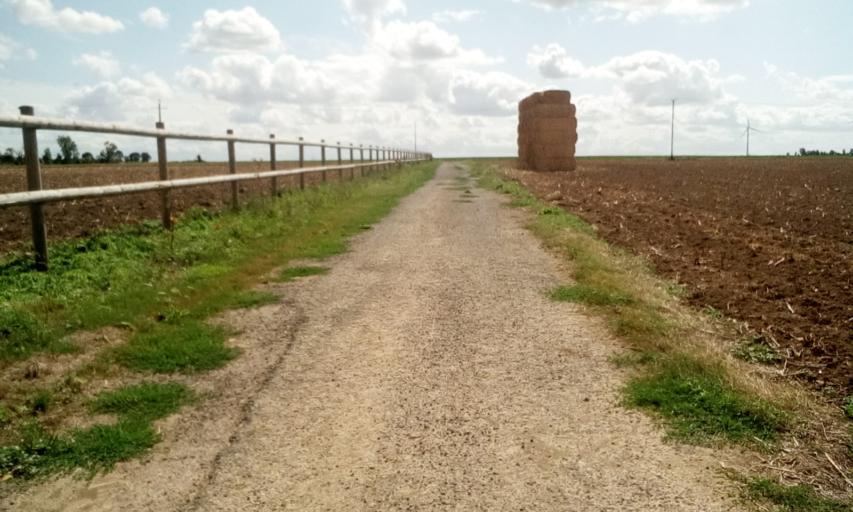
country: FR
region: Lower Normandy
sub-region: Departement du Calvados
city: Bellengreville
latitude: 49.1075
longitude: -0.2086
